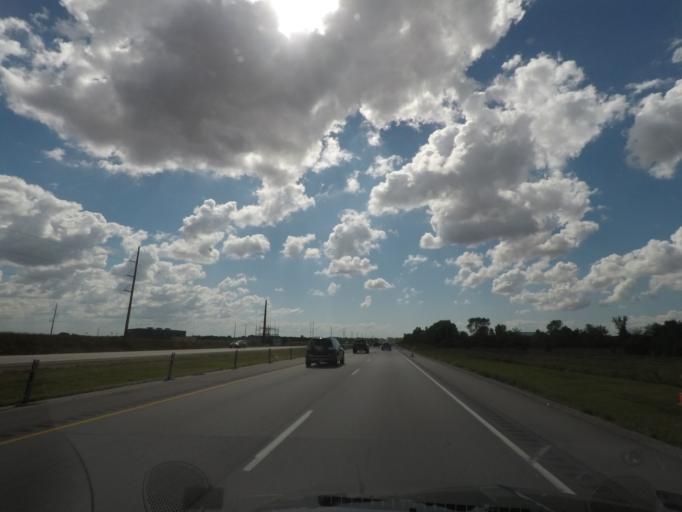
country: US
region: Iowa
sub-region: Story County
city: Huxley
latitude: 41.9193
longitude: -93.5704
